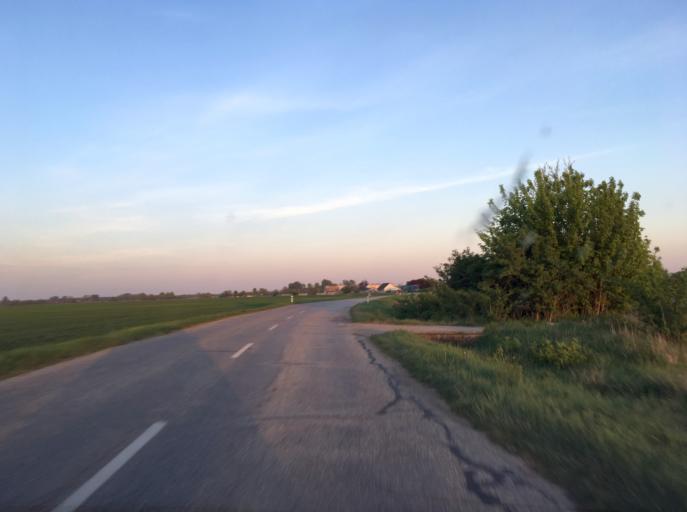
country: SK
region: Nitriansky
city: Kolarovo
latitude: 47.9019
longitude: 17.9589
